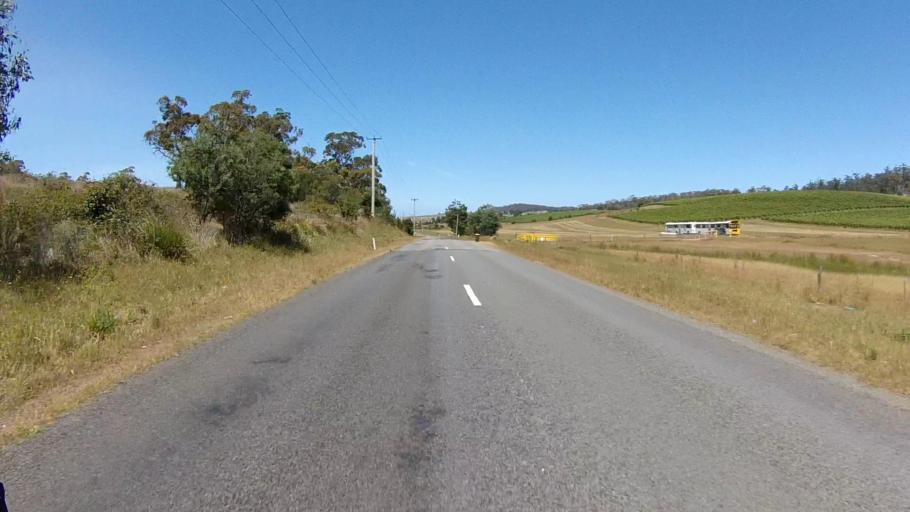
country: AU
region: Tasmania
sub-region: Clarence
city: Howrah
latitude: -42.8719
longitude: 147.4254
